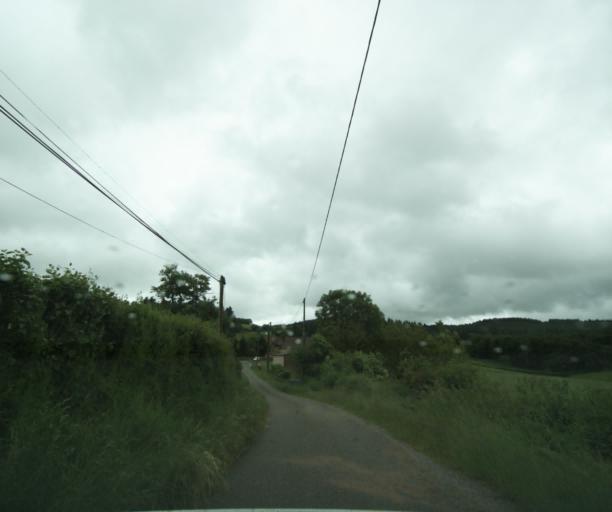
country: FR
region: Bourgogne
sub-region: Departement de Saone-et-Loire
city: Matour
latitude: 46.4544
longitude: 4.4607
